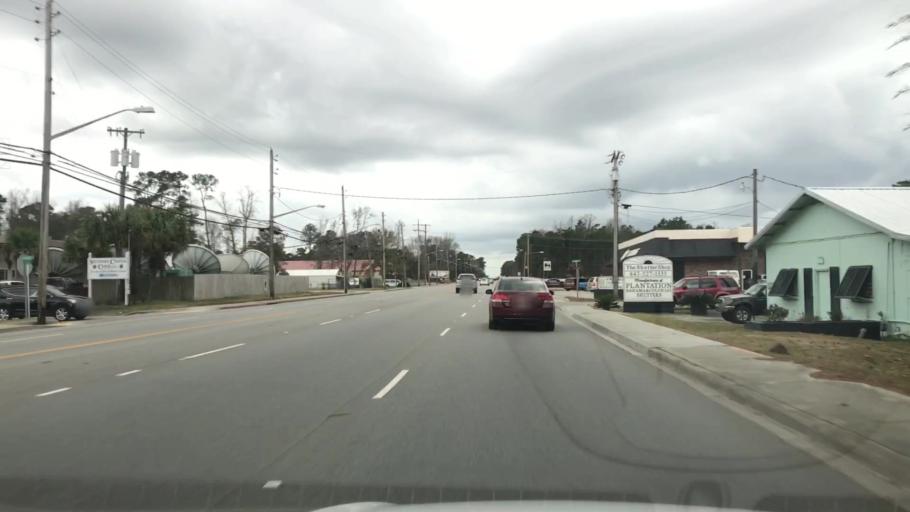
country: US
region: South Carolina
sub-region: Georgetown County
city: Georgetown
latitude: 33.3454
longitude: -79.2977
